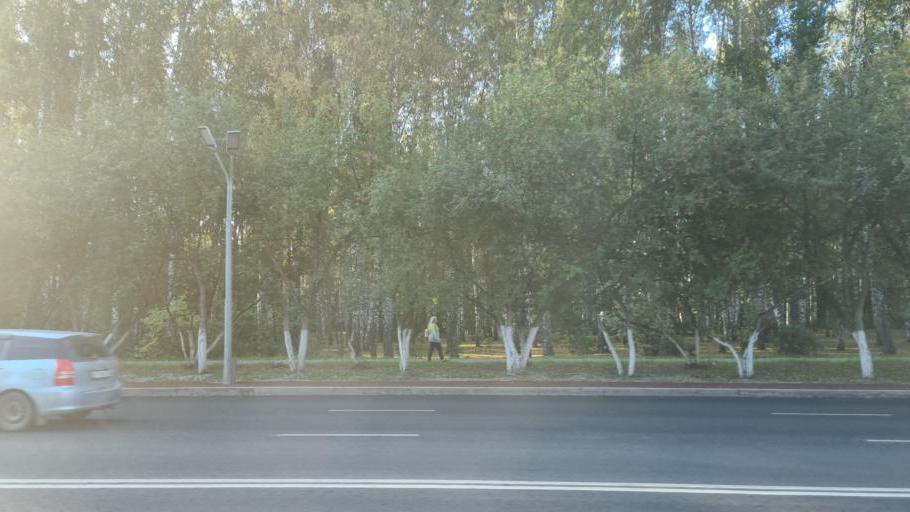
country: RU
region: Tomsk
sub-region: Tomskiy Rayon
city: Tomsk
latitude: 56.4552
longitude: 84.9527
